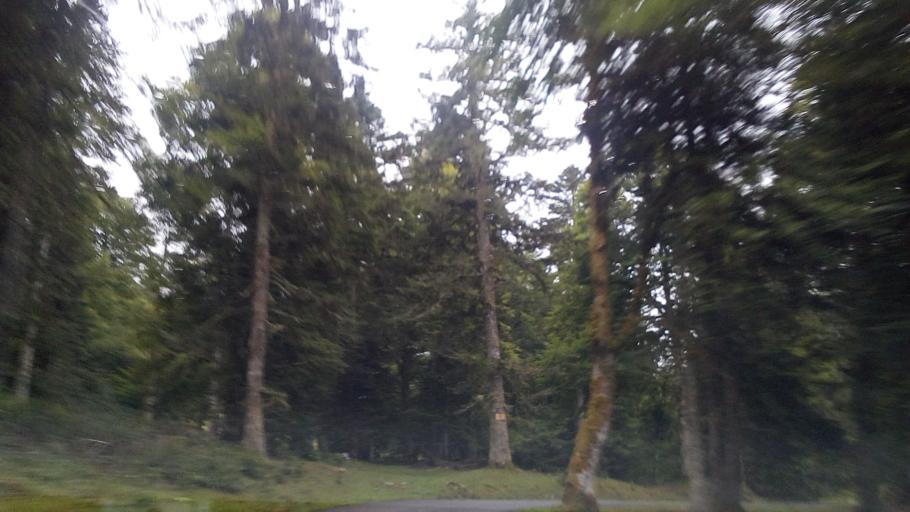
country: FR
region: Midi-Pyrenees
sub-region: Departement des Hautes-Pyrenees
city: Saint-Lary-Soulan
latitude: 42.9224
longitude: 0.2933
